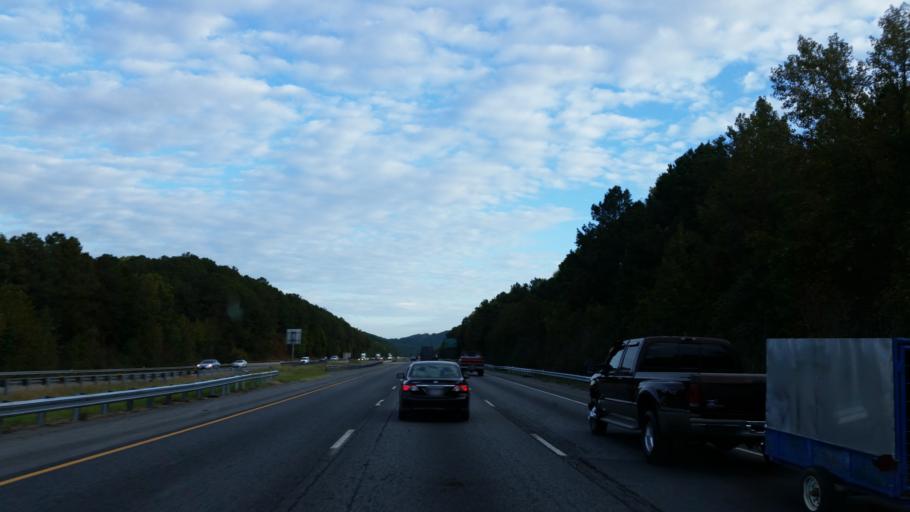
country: US
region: Georgia
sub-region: Bartow County
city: Emerson
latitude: 34.1594
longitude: -84.7536
